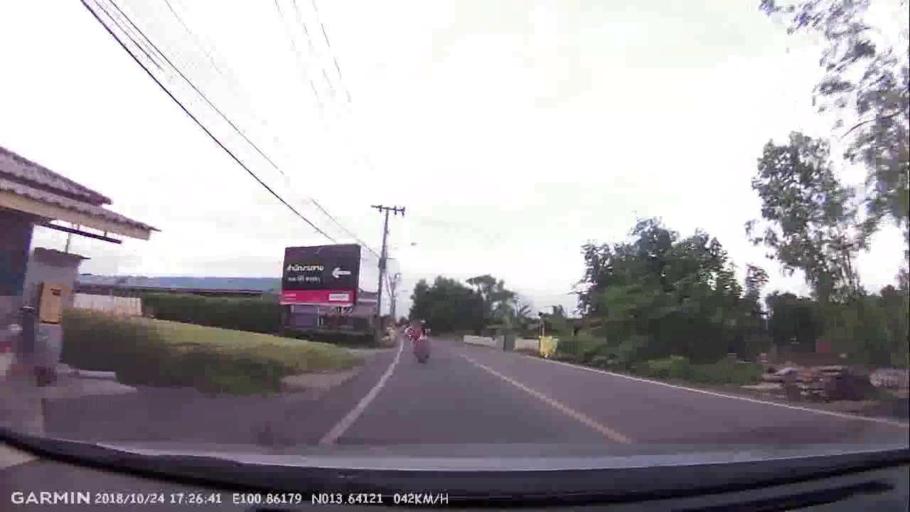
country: TH
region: Samut Prakan
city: Ban Khlong Bang Sao Thong
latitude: 13.6413
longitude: 100.8617
